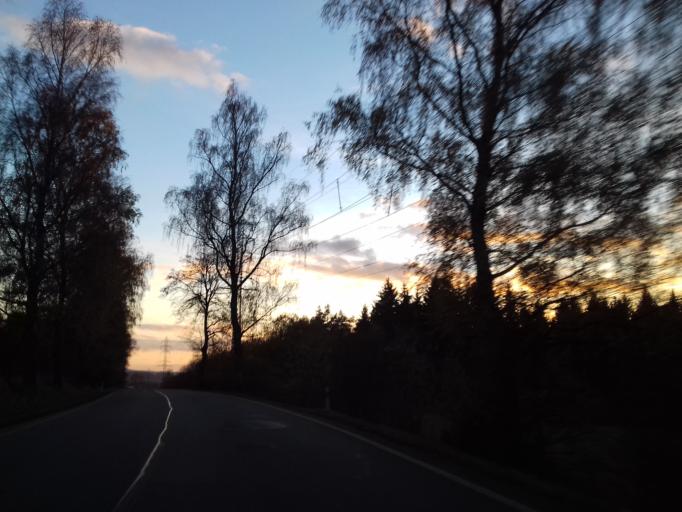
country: CZ
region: Pardubicky
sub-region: Okres Chrudim
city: Hlinsko
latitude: 49.7383
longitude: 15.8786
